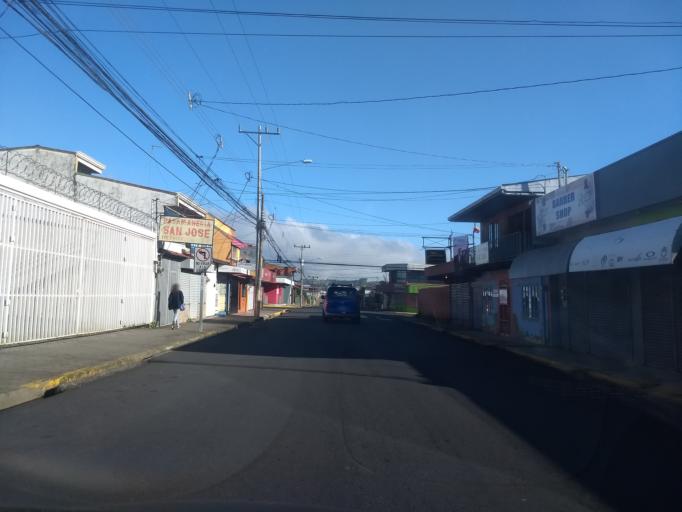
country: CR
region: Alajuela
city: San Ramon
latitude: 10.0888
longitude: -84.4687
